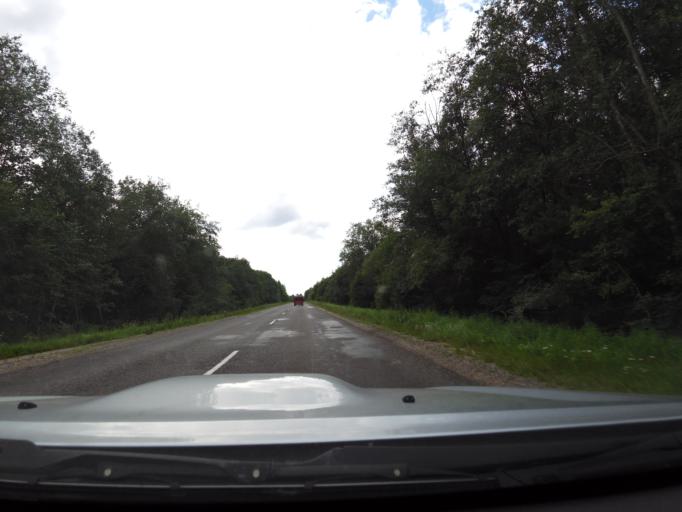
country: LV
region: Akniste
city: Akniste
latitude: 56.0079
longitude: 25.9399
